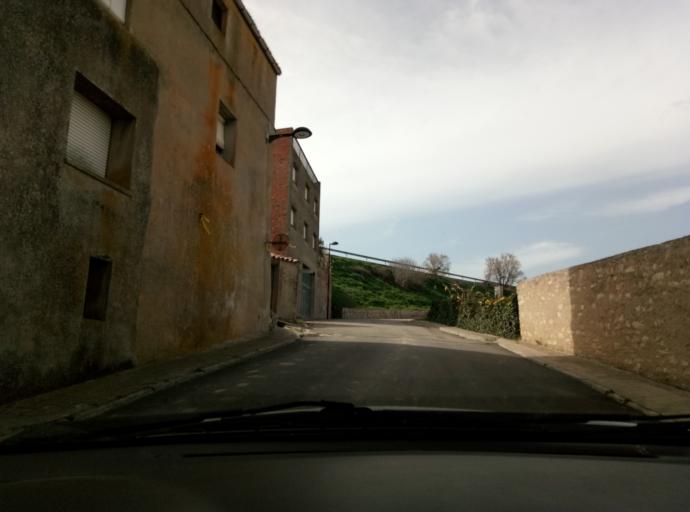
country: ES
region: Catalonia
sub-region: Provincia de Lleida
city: Sant Guim de Freixenet
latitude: 41.6262
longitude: 1.4145
